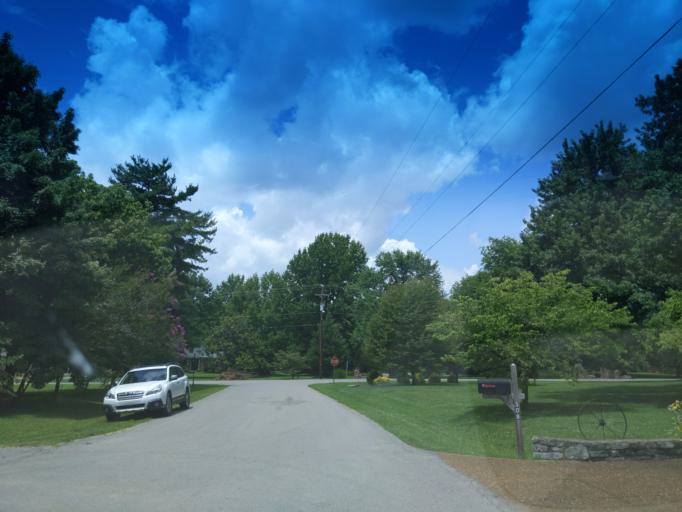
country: US
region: Tennessee
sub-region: Williamson County
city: Brentwood Estates
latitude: 36.0182
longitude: -86.7784
